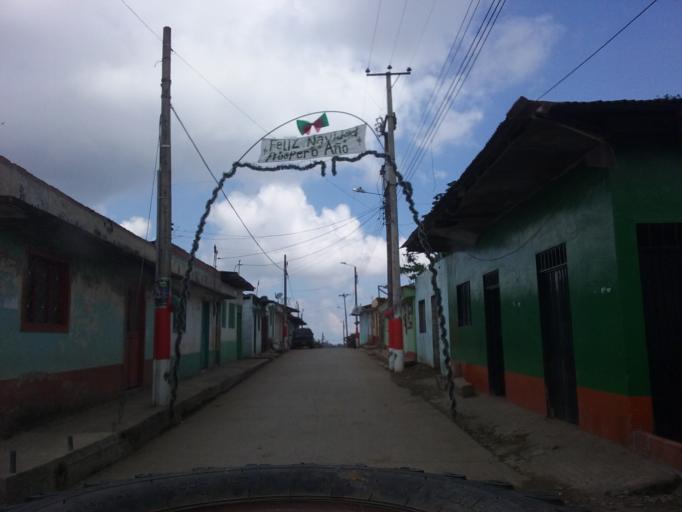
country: CO
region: Tolima
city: Libano
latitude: 4.7994
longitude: -75.0495
